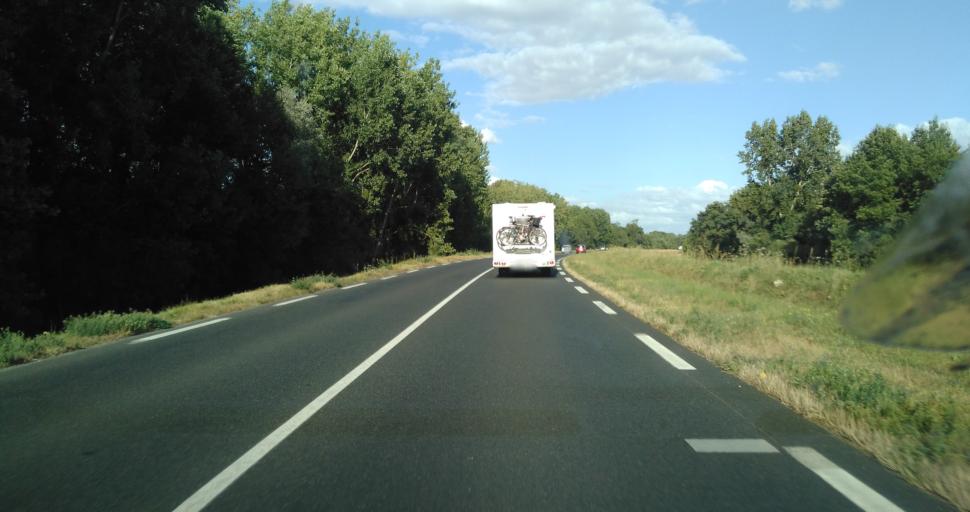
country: FR
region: Centre
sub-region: Departement d'Indre-et-Loire
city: Noizay
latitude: 47.4041
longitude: 0.8865
